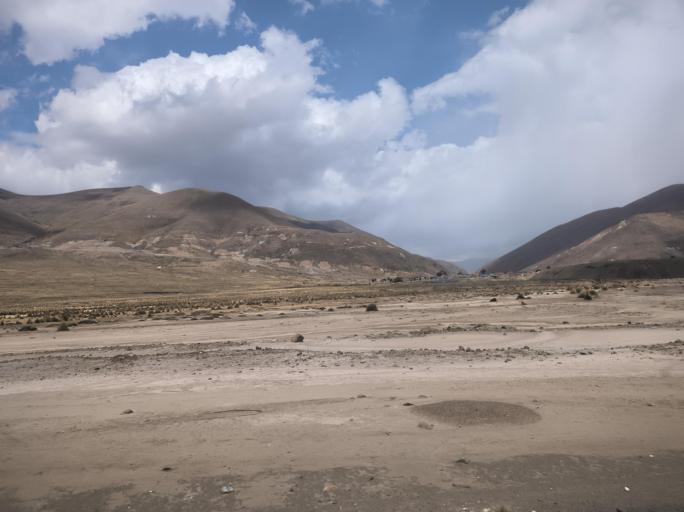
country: BO
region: Oruro
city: Poopo
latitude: -18.3769
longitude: -66.9798
